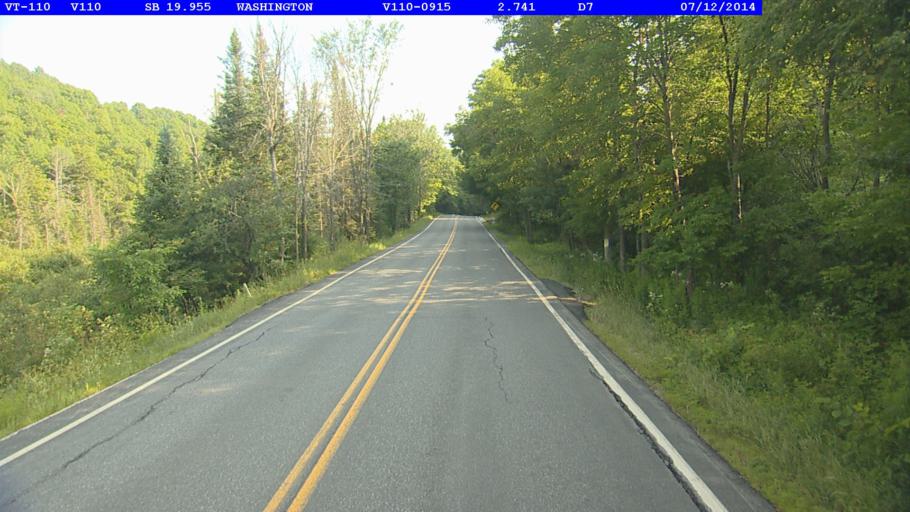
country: US
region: Vermont
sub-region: Orange County
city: Chelsea
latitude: 44.0743
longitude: -72.4618
